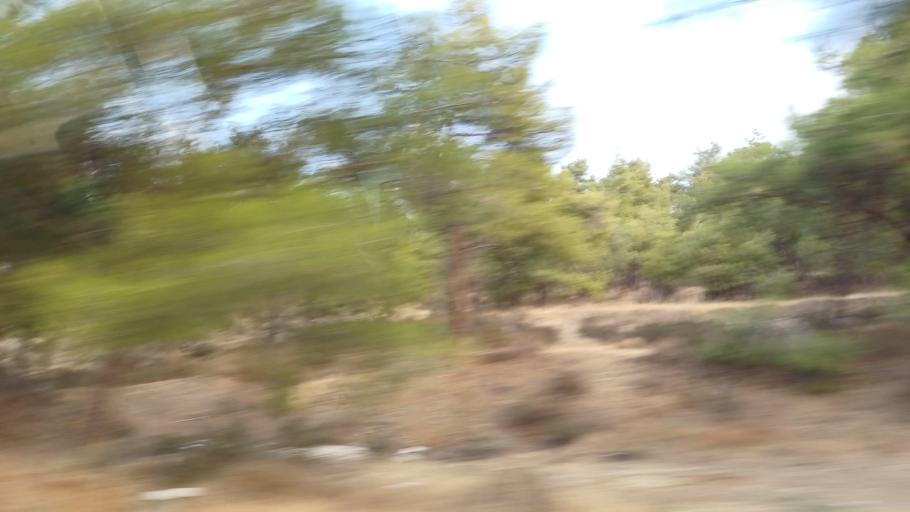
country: CY
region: Lefkosia
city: Kakopetria
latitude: 35.0605
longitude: 32.9137
